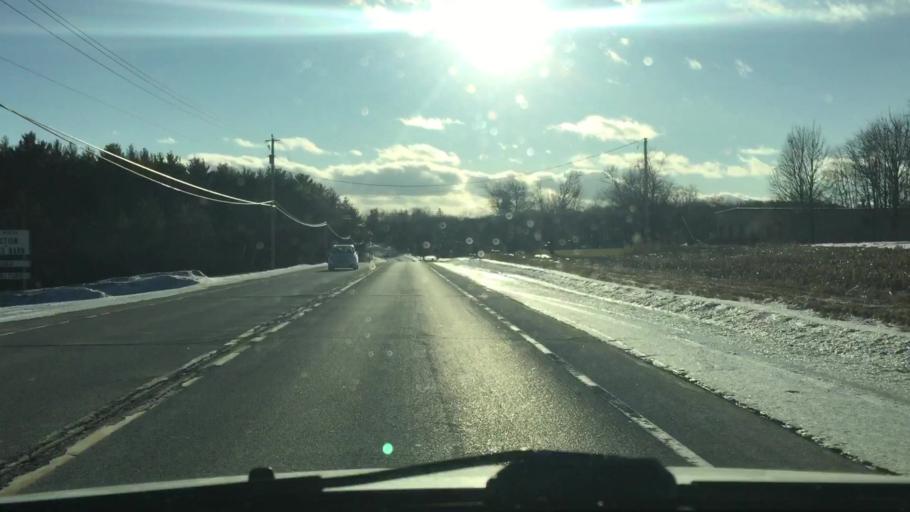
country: US
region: Wisconsin
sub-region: Waukesha County
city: New Berlin
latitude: 42.9605
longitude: -88.1348
